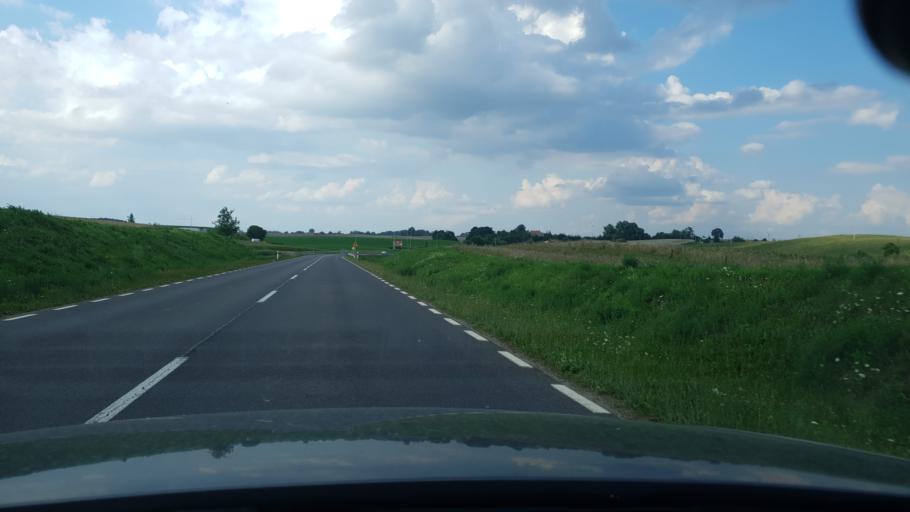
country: PL
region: Kujawsko-Pomorskie
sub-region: Powiat wabrzeski
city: Wabrzezno
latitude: 53.3004
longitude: 18.9267
